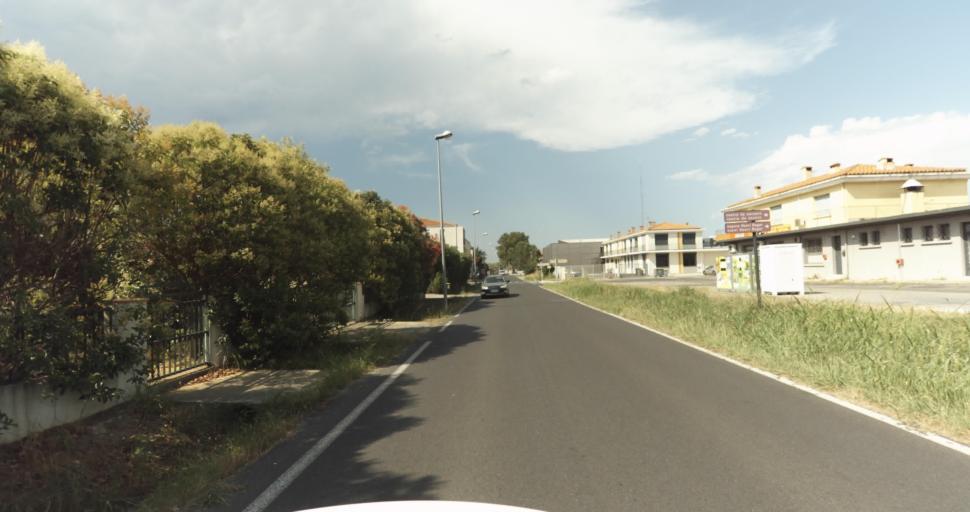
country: FR
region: Languedoc-Roussillon
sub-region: Departement des Pyrenees-Orientales
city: Elne
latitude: 42.6043
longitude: 2.9736
